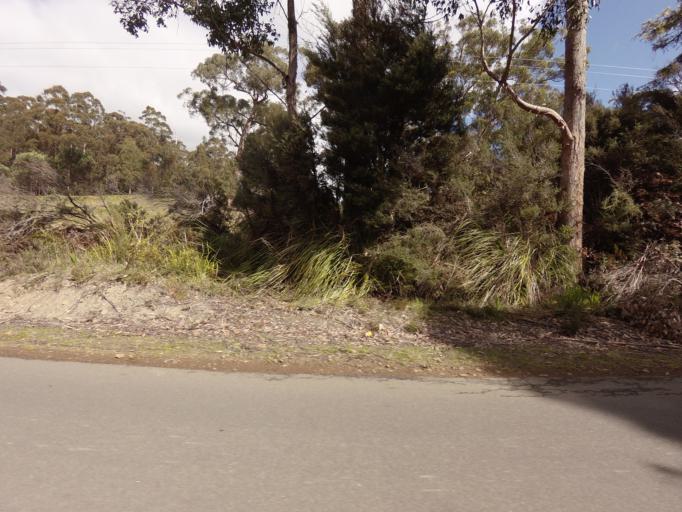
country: AU
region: Tasmania
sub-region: Huon Valley
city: Geeveston
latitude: -43.4152
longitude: 146.9632
